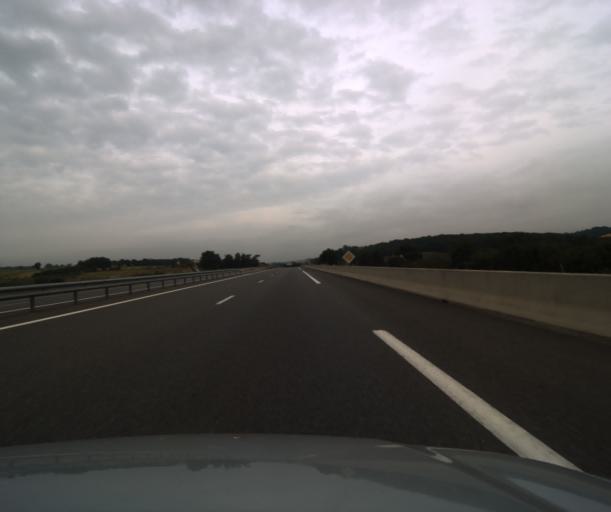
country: FR
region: Midi-Pyrenees
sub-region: Departement du Gers
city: Aubiet
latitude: 43.6570
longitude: 0.7783
